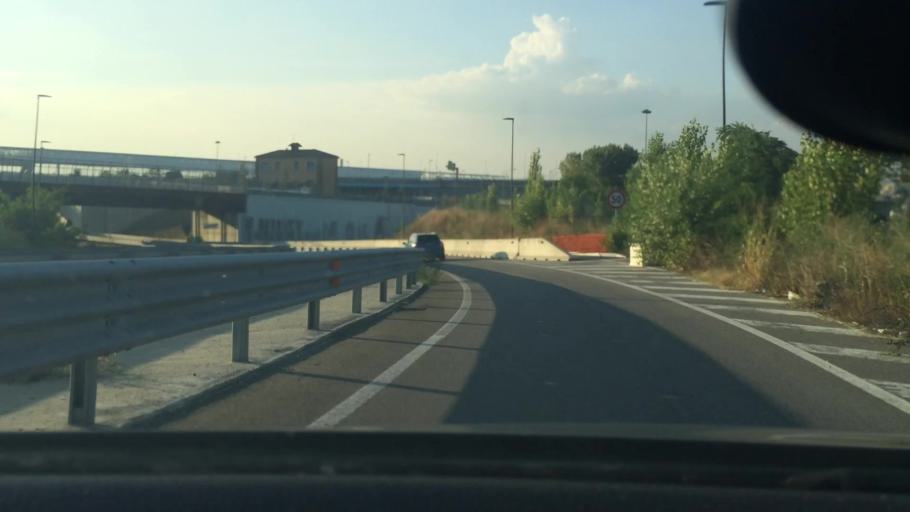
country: IT
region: Lombardy
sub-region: Citta metropolitana di Milano
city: Baranzate
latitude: 45.5122
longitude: 9.1066
